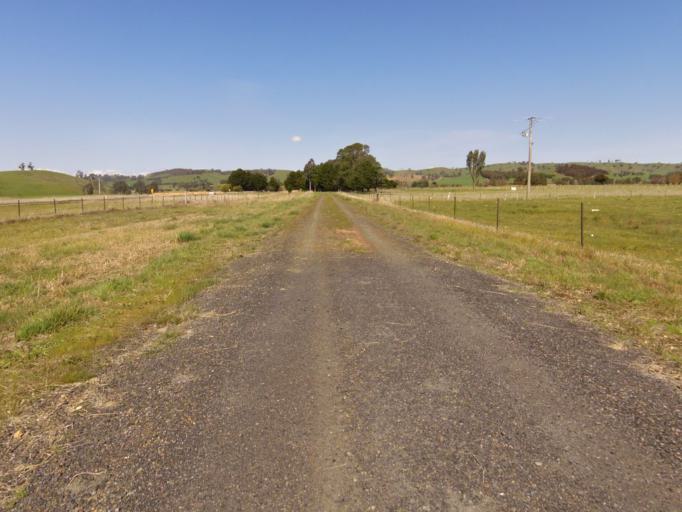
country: AU
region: Victoria
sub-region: Murrindindi
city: Alexandra
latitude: -37.0062
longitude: 145.7502
